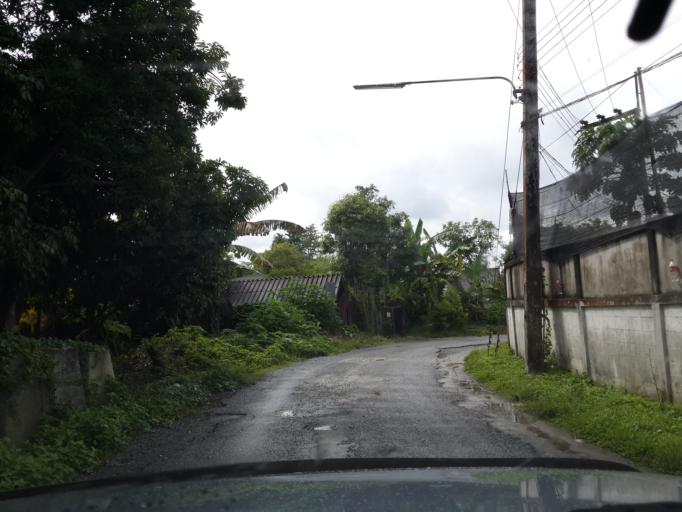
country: TH
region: Narathiwat
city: Rueso
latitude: 6.3862
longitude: 101.5153
